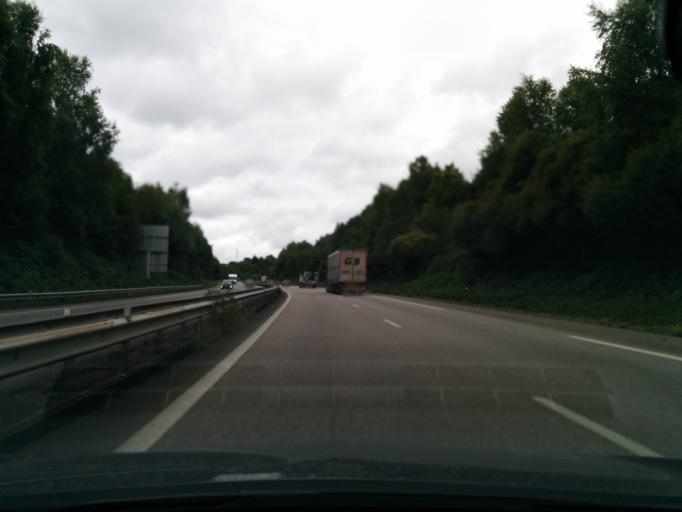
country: FR
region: Limousin
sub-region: Departement de la Haute-Vienne
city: Bonnac-la-Cote
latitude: 45.9282
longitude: 1.3033
